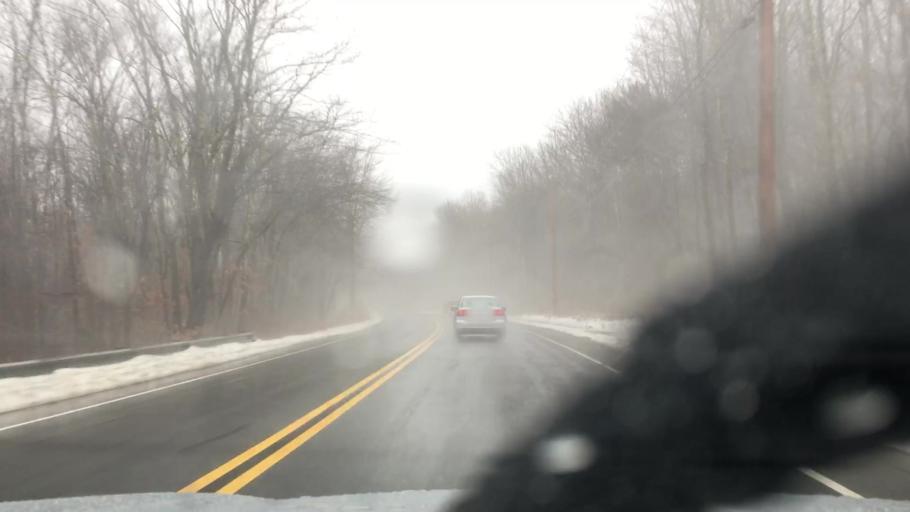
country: US
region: Massachusetts
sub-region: Hampden County
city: Ludlow
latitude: 42.2033
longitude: -72.4933
